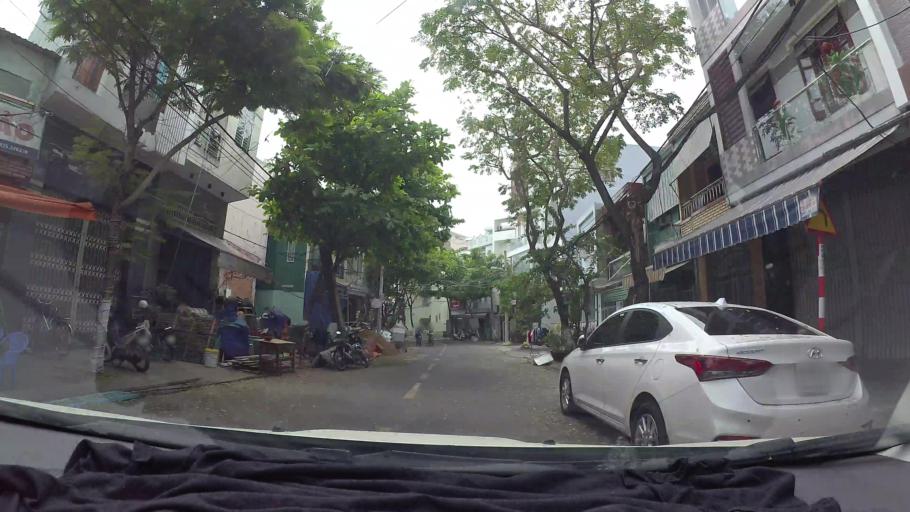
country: VN
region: Da Nang
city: Da Nang
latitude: 16.0840
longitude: 108.2156
